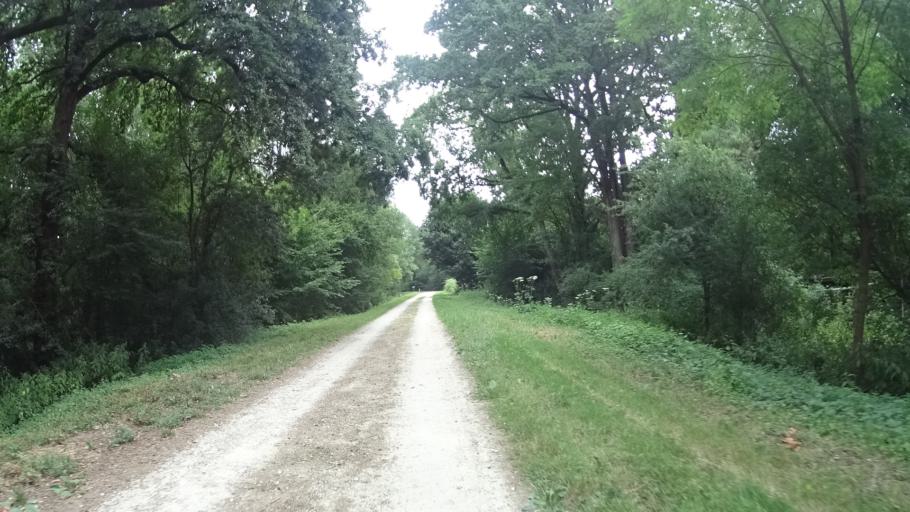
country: FR
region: Centre
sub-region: Departement d'Indre-et-Loire
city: Huismes
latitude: 47.2564
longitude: 0.2629
